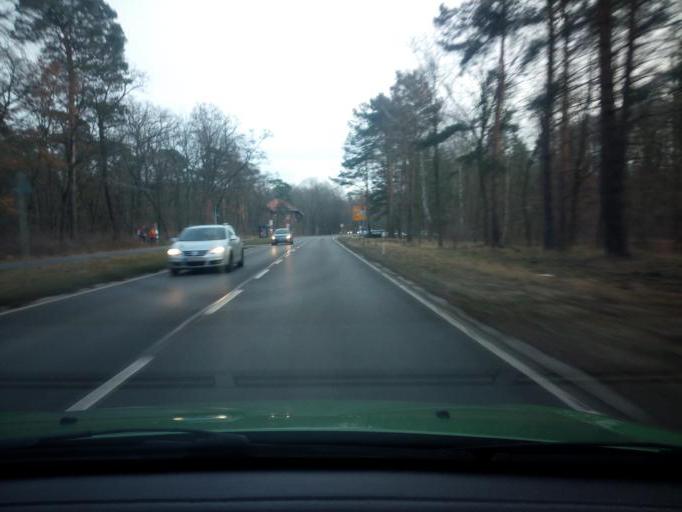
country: DE
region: Berlin
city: Friedrichshagen
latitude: 52.4311
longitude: 13.6128
